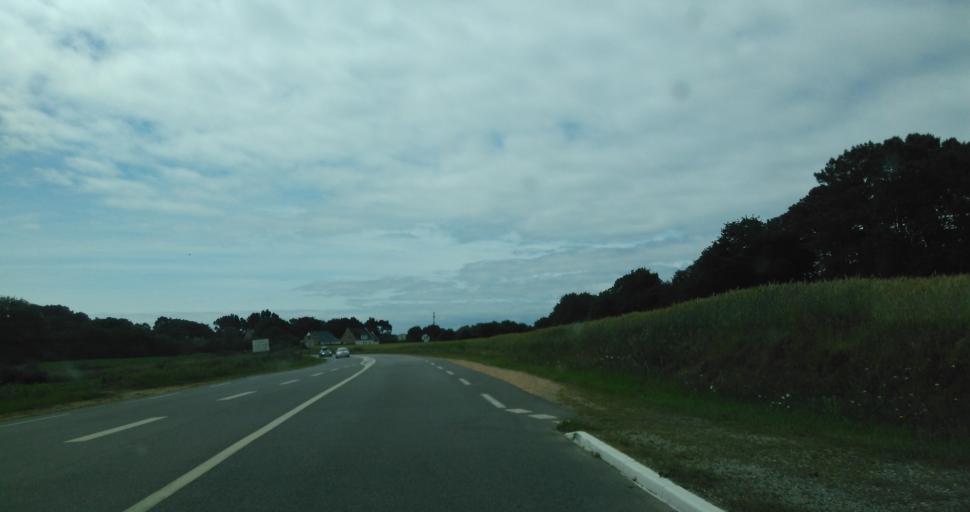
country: FR
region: Brittany
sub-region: Departement du Morbihan
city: La Trinite-sur-Mer
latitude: 47.6028
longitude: -3.0435
